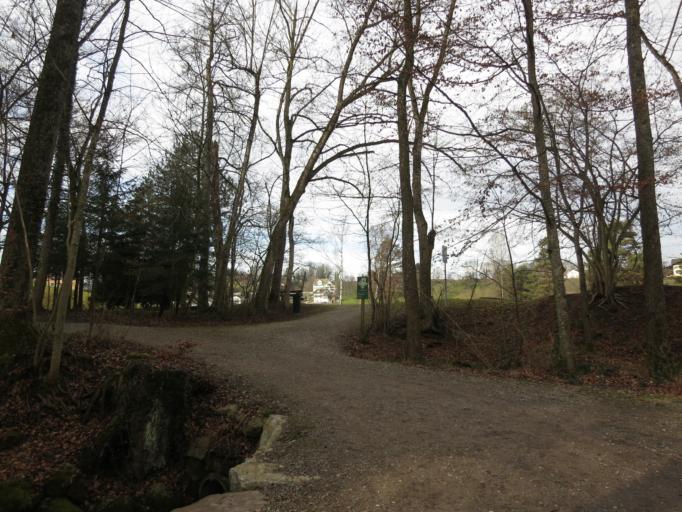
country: CH
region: Zurich
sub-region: Bezirk Meilen
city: Uerikon
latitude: 47.2393
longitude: 8.7646
